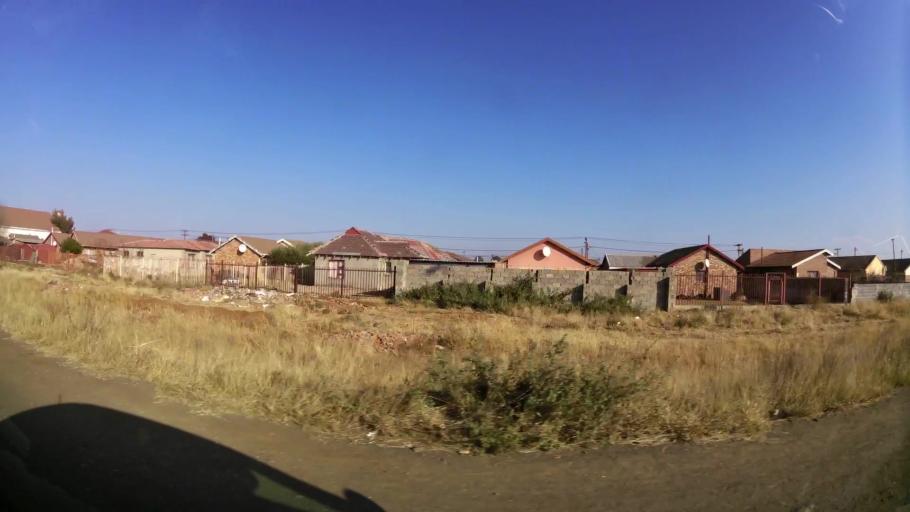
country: ZA
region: Orange Free State
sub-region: Mangaung Metropolitan Municipality
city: Bloemfontein
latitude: -29.1497
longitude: 26.2654
